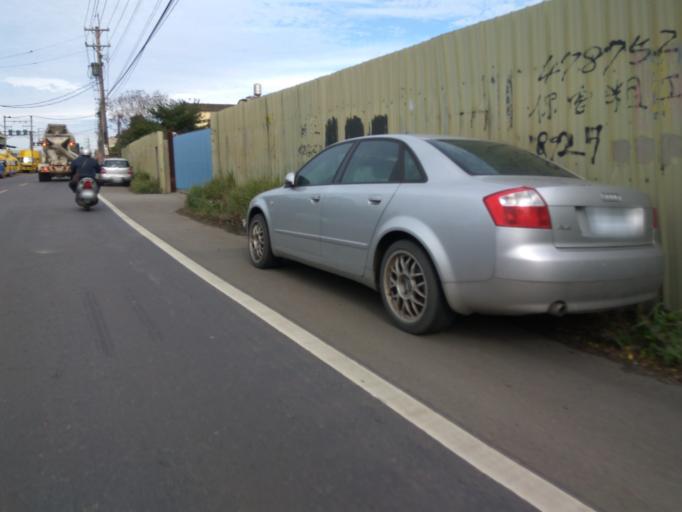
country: TW
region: Taiwan
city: Daxi
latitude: 24.9400
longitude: 121.1595
